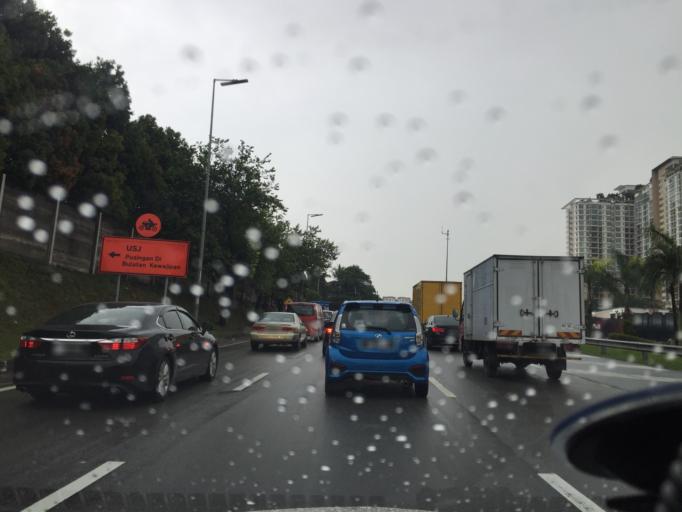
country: MY
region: Selangor
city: Subang Jaya
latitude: 3.0633
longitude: 101.5920
